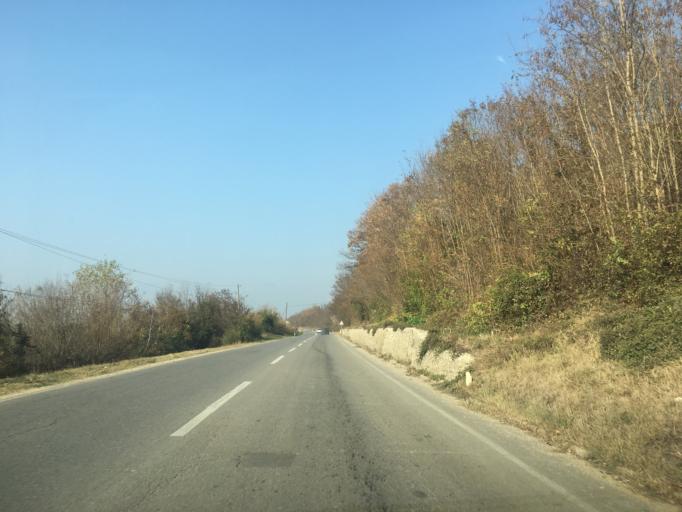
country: XK
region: Pec
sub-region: Komuna e Pejes
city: Kosuriq
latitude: 42.6417
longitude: 20.4203
